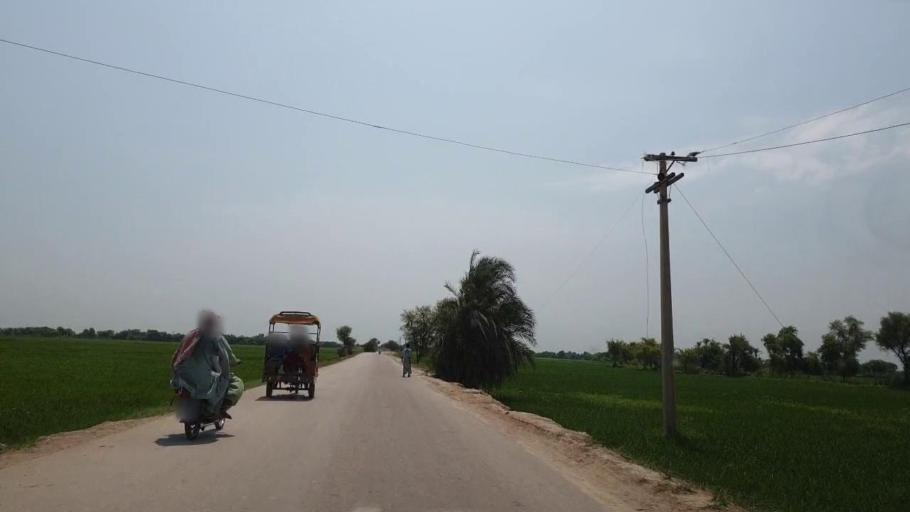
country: PK
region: Sindh
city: Ratodero
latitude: 27.8227
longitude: 68.2430
